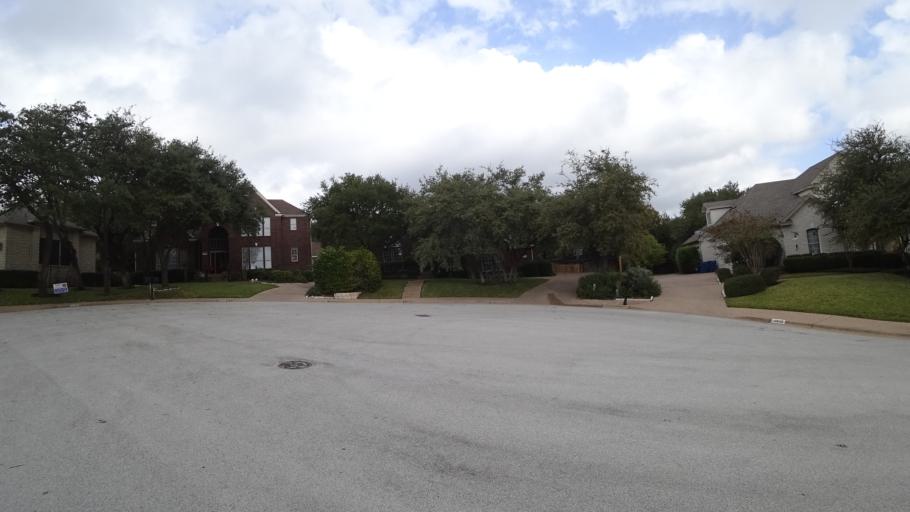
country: US
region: Texas
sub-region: Travis County
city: Barton Creek
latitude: 30.3104
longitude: -97.8995
